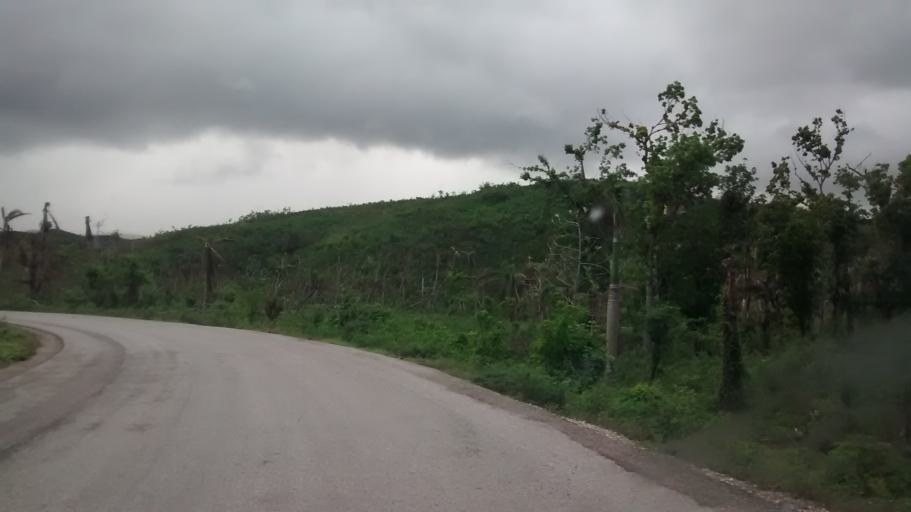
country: HT
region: Grandans
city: Jeremie
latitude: 18.6177
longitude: -74.0886
